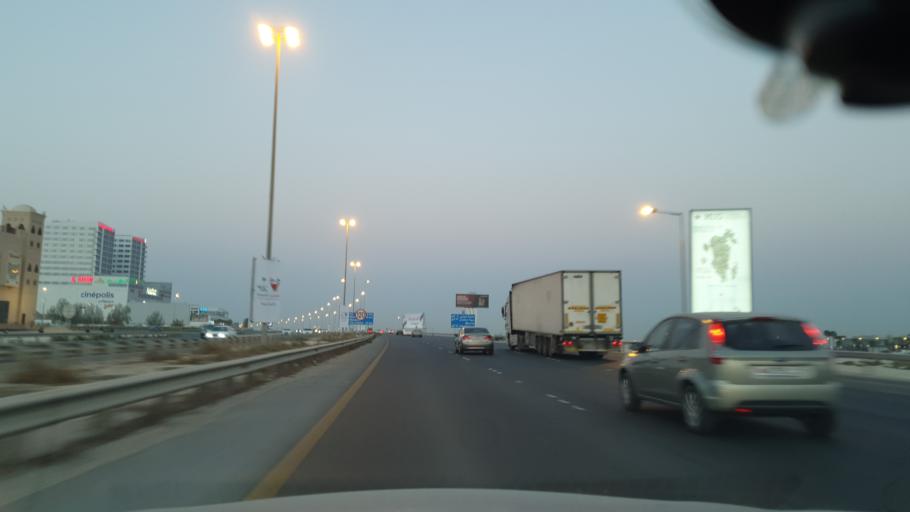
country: BH
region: Central Governorate
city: Madinat Hamad
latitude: 26.1735
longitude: 50.4803
